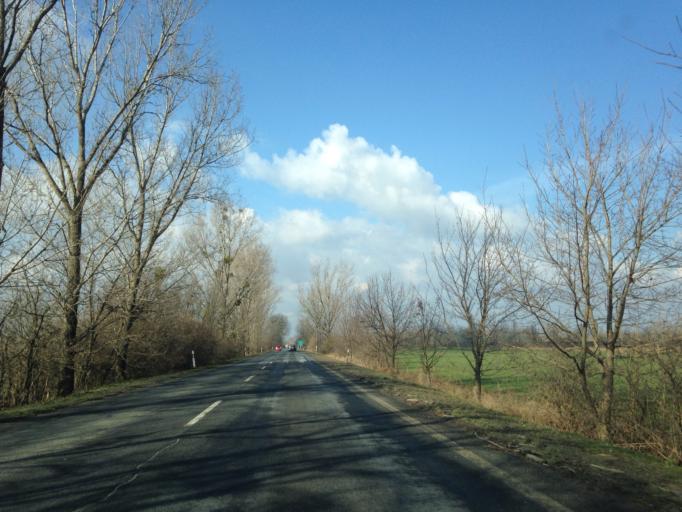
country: HU
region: Komarom-Esztergom
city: Almasfuzito
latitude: 47.7153
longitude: 18.2813
